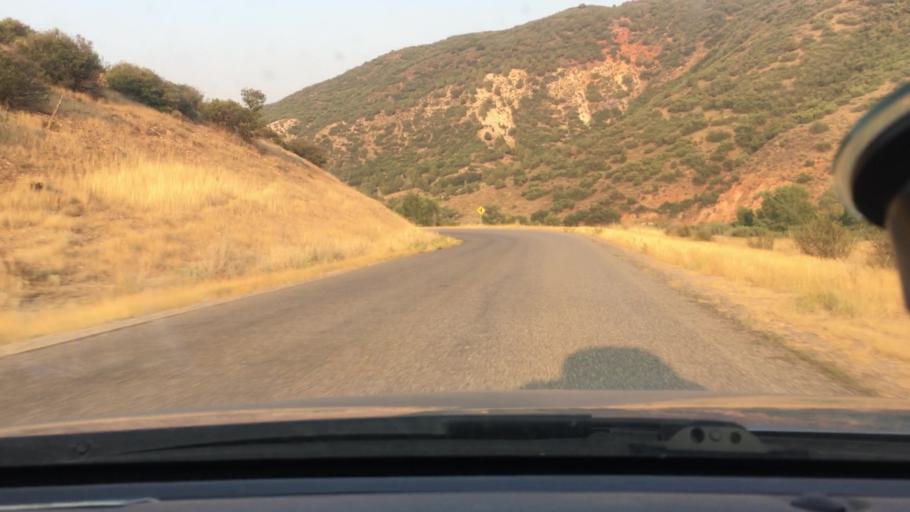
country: US
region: Utah
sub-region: Utah County
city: Mapleton
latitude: 40.0472
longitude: -111.4714
